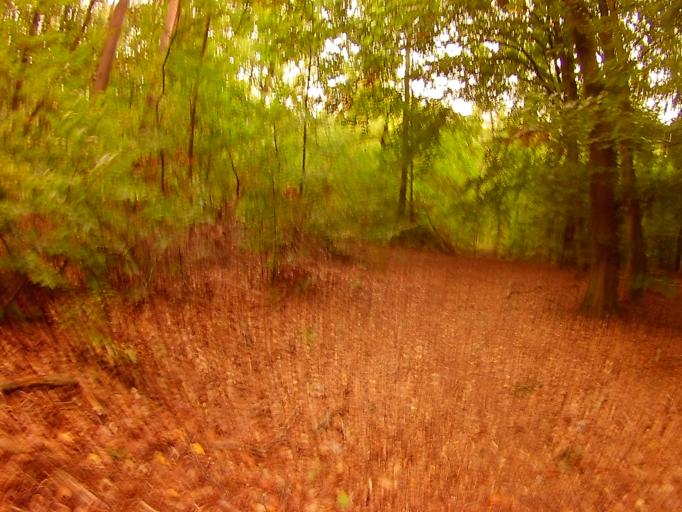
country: DE
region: Brandenburg
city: Zeuthen
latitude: 52.4002
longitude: 13.6189
